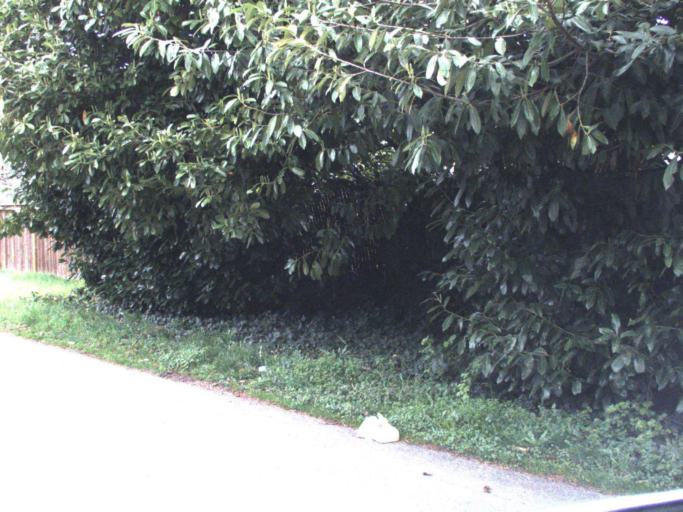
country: US
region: Washington
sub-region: King County
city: Normandy Park
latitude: 47.4353
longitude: -122.3352
